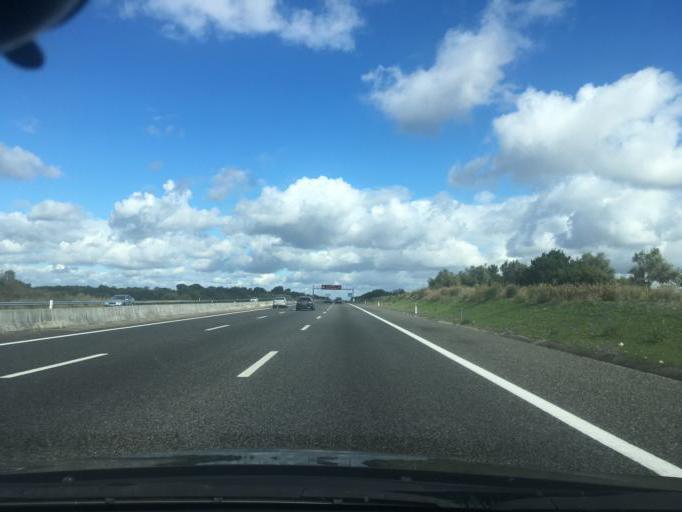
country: PT
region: Santarem
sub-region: Cartaxo
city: Pontevel
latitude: 39.1836
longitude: -8.8283
